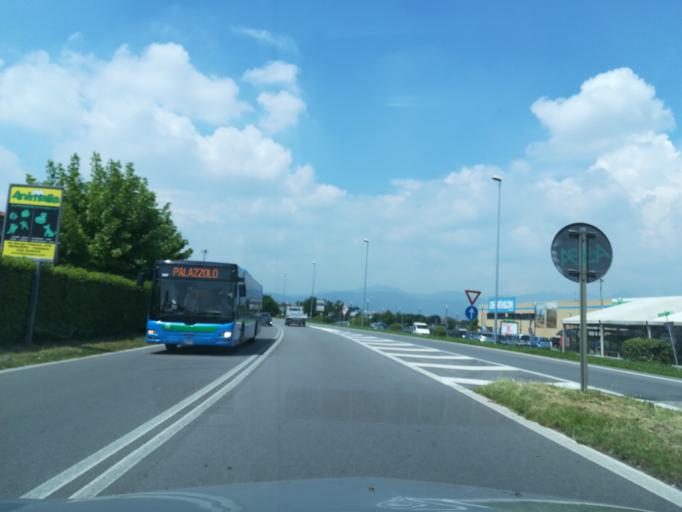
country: IT
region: Lombardy
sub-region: Provincia di Bergamo
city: Seriate
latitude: 45.6697
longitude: 9.7385
